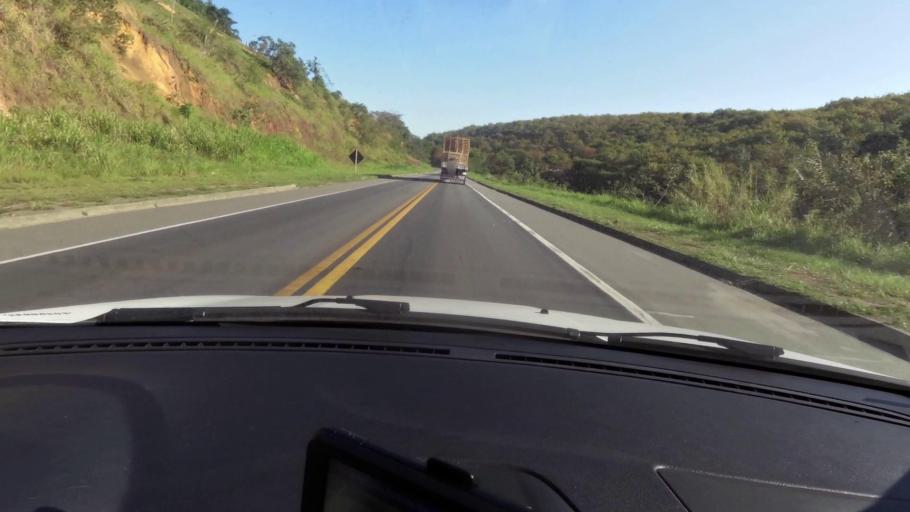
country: BR
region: Espirito Santo
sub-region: Alfredo Chaves
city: Alfredo Chaves
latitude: -20.6788
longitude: -40.6669
